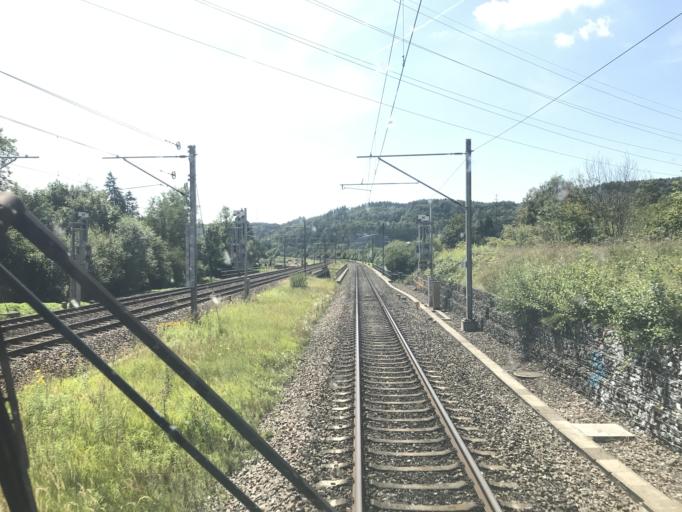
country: CH
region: Zurich
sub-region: Bezirk Winterthur
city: Toess (Kreis 4) / Eichliacker
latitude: 47.4822
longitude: 8.7089
